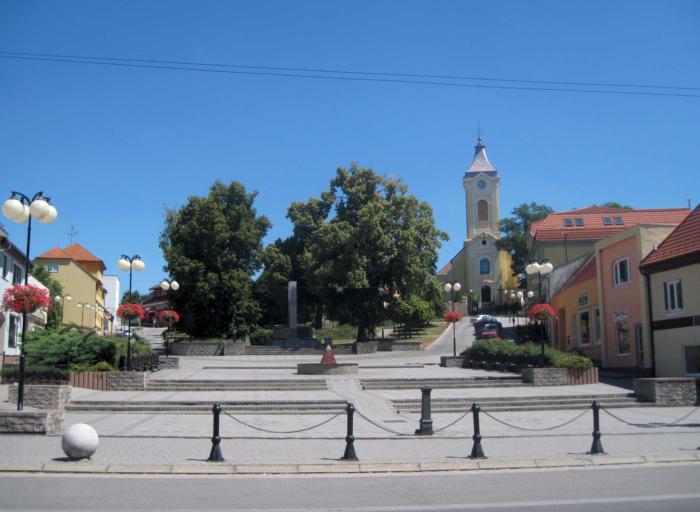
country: SK
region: Trnavsky
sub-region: Okres Skalica
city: Holic
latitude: 48.8082
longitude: 17.1622
